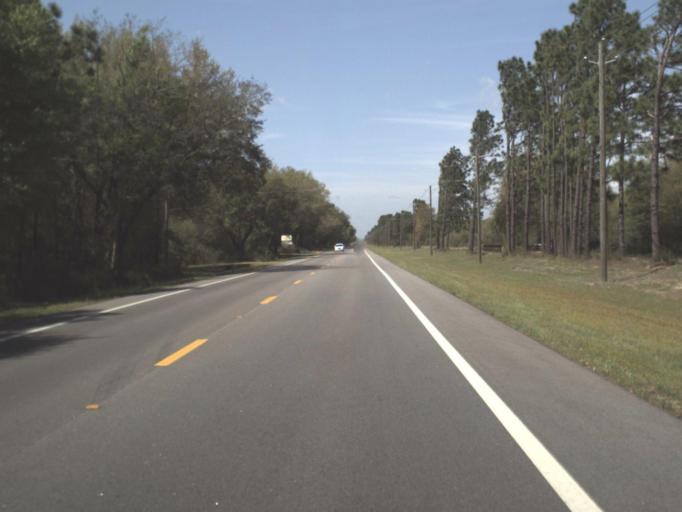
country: US
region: Florida
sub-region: Santa Rosa County
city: East Milton
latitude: 30.6429
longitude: -86.9371
